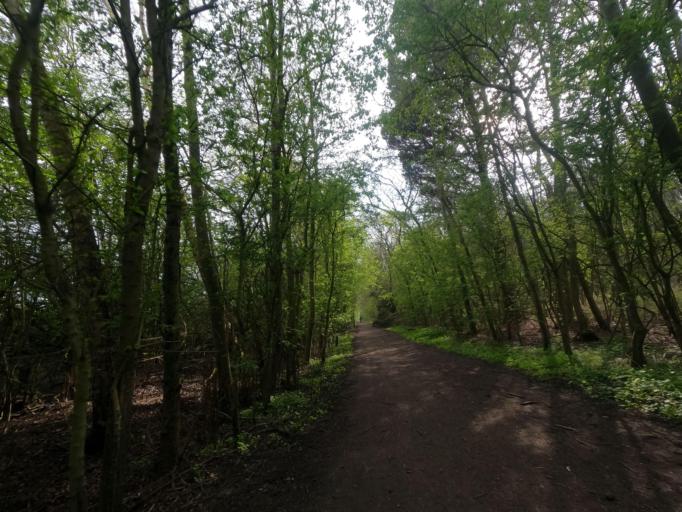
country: GB
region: England
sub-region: Newcastle upon Tyne
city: Hazlerigg
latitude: 55.0391
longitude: -1.6472
